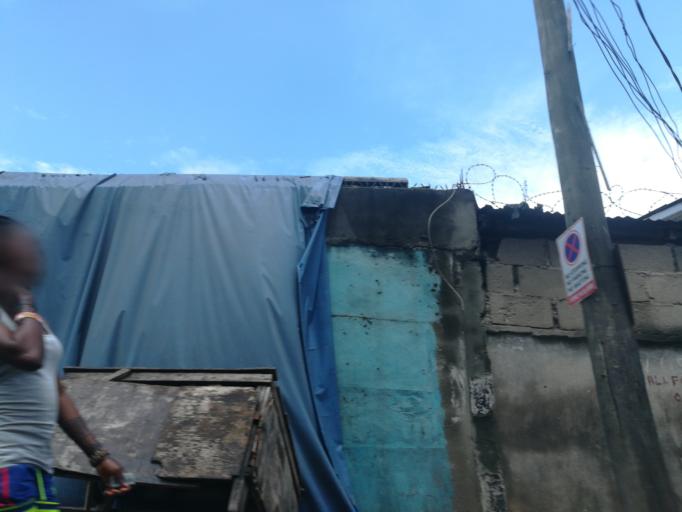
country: NG
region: Lagos
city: Somolu
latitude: 6.5624
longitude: 3.3688
